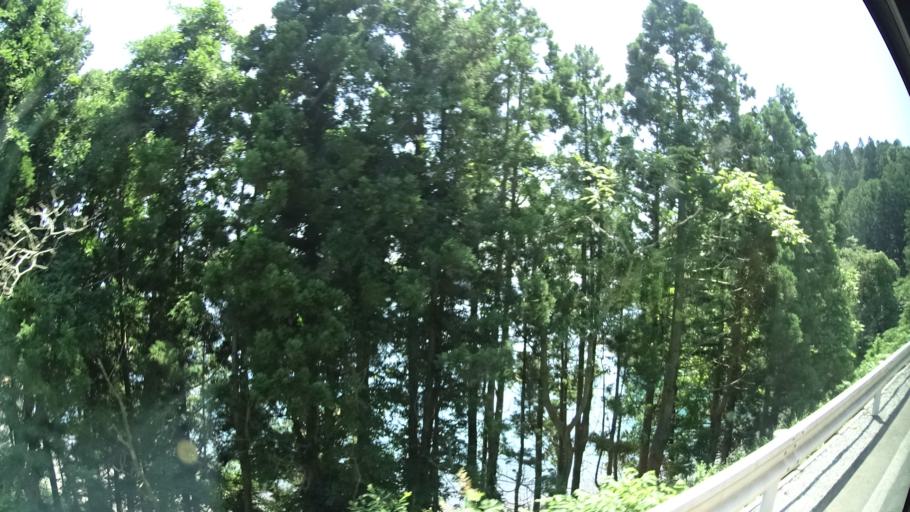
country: JP
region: Iwate
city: Ofunato
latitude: 38.9918
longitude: 141.7118
